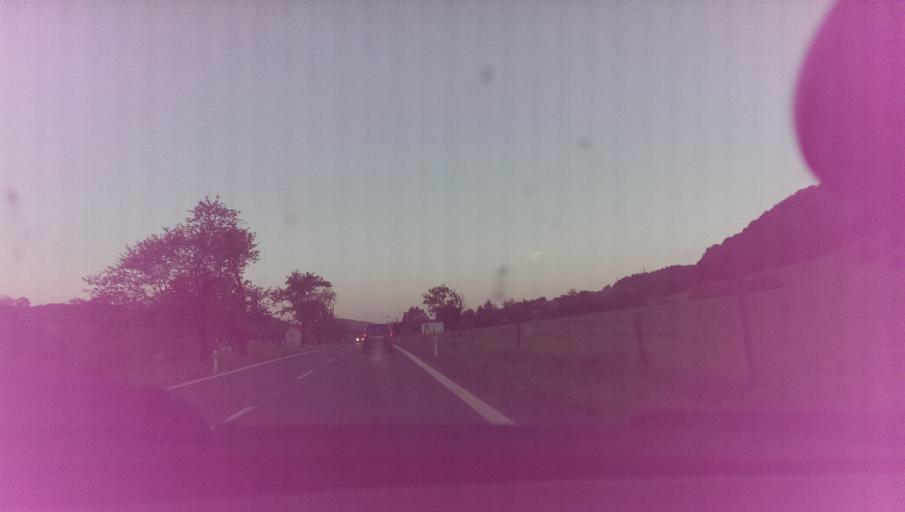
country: CZ
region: Zlin
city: Valasska Polanka
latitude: 49.2960
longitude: 18.0011
